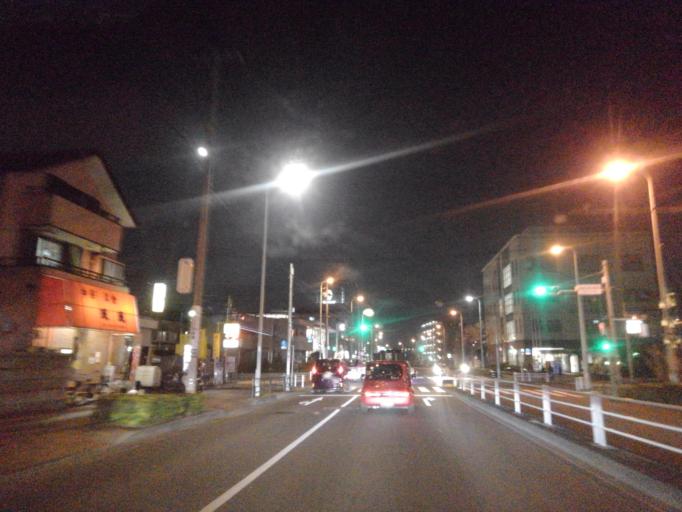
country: JP
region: Tokyo
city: Chofugaoka
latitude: 35.6382
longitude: 139.5051
